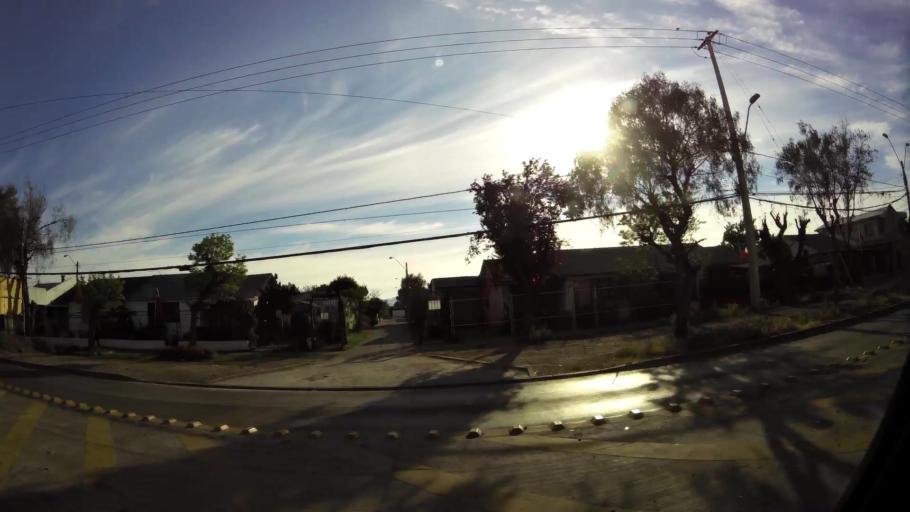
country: CL
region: Santiago Metropolitan
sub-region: Provincia de Santiago
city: Lo Prado
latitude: -33.4481
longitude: -70.7072
